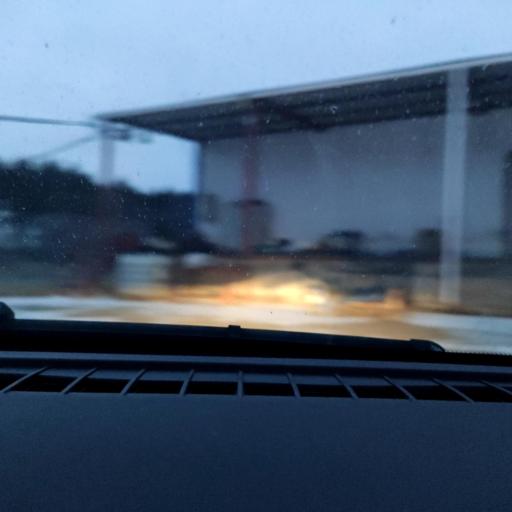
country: RU
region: Voronezj
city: Voronezh
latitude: 51.6744
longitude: 39.2751
